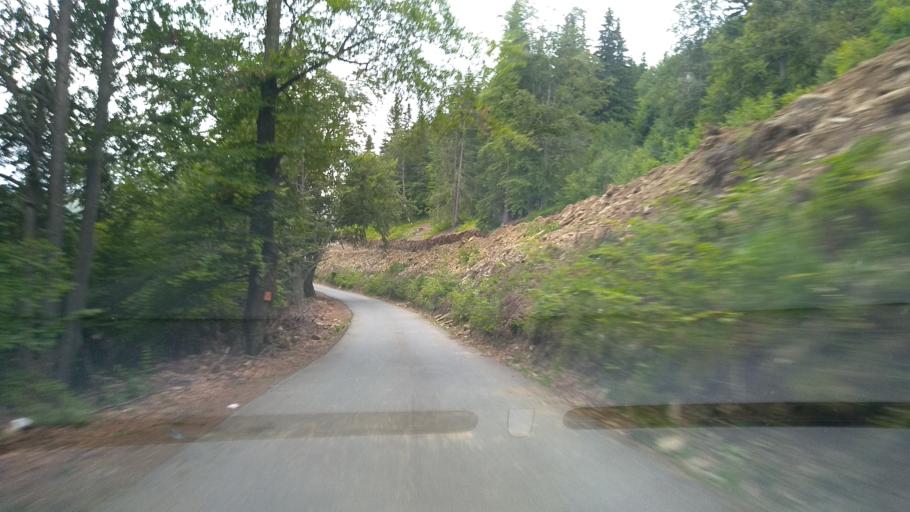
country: RO
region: Hunedoara
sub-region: Municipiul  Vulcan
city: Jiu-Paroseni
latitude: 45.3239
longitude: 23.2921
